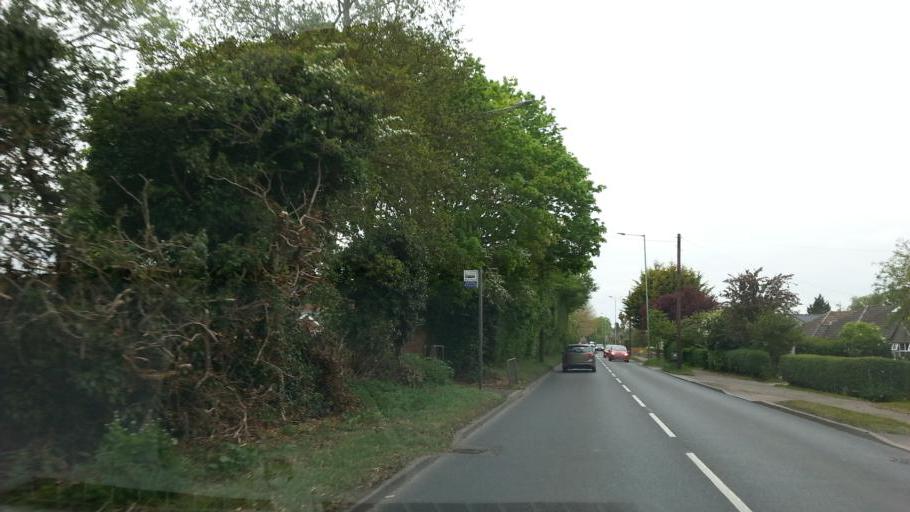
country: GB
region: England
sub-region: Suffolk
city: Bury St Edmunds
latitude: 52.2291
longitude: 0.7313
